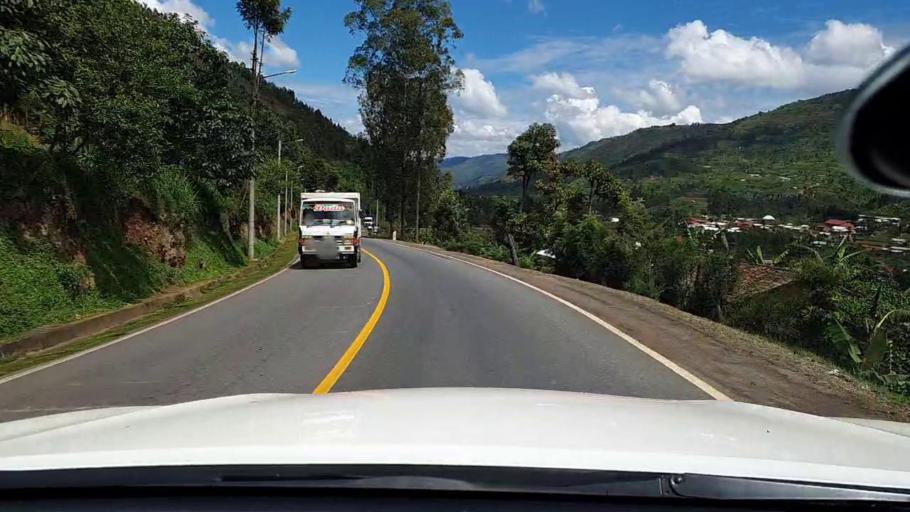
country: RW
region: Kigali
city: Kigali
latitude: -1.7703
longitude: 29.9289
